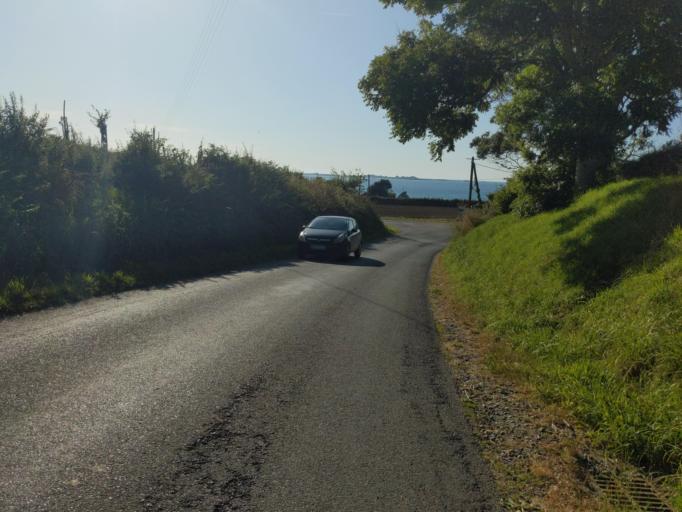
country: FR
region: Brittany
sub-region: Departement des Cotes-d'Armor
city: Pleubian
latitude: 48.8529
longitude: -3.1420
